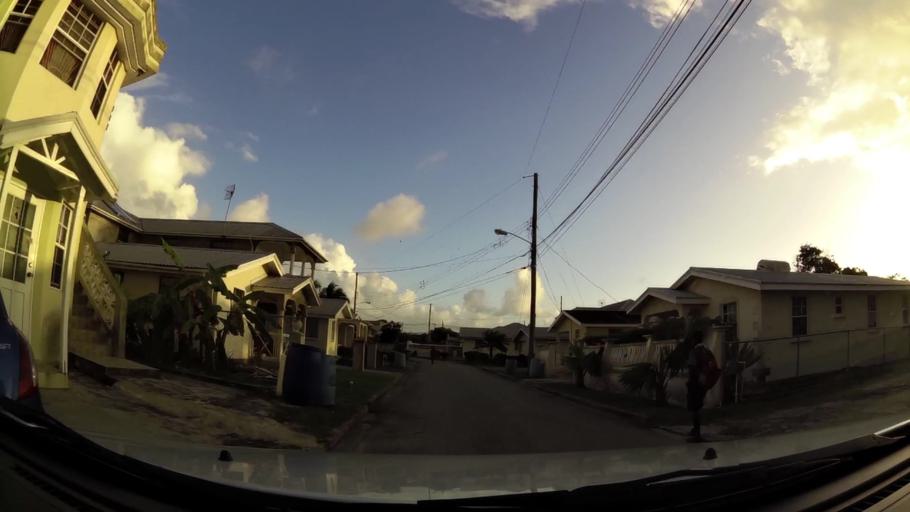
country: BB
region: Saint Philip
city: Crane
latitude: 13.1062
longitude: -59.4710
